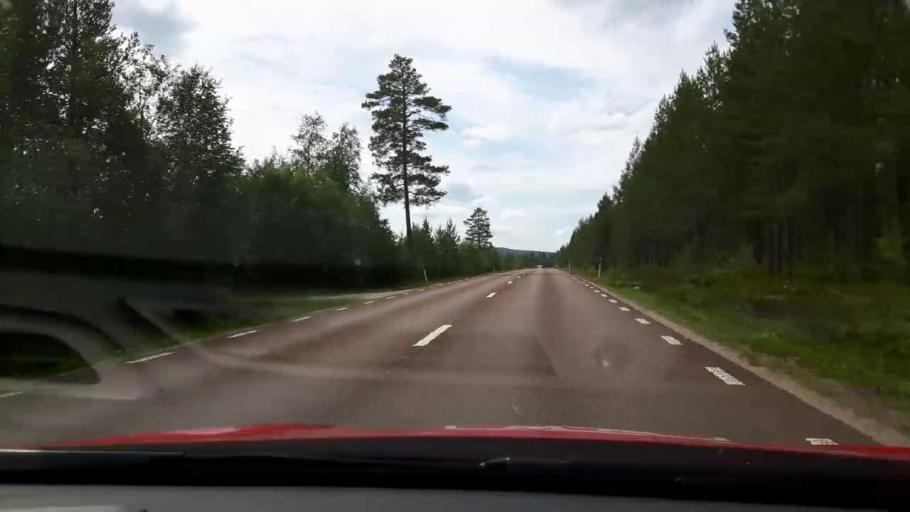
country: SE
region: Jaemtland
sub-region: Harjedalens Kommun
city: Sveg
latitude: 62.0440
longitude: 14.4718
